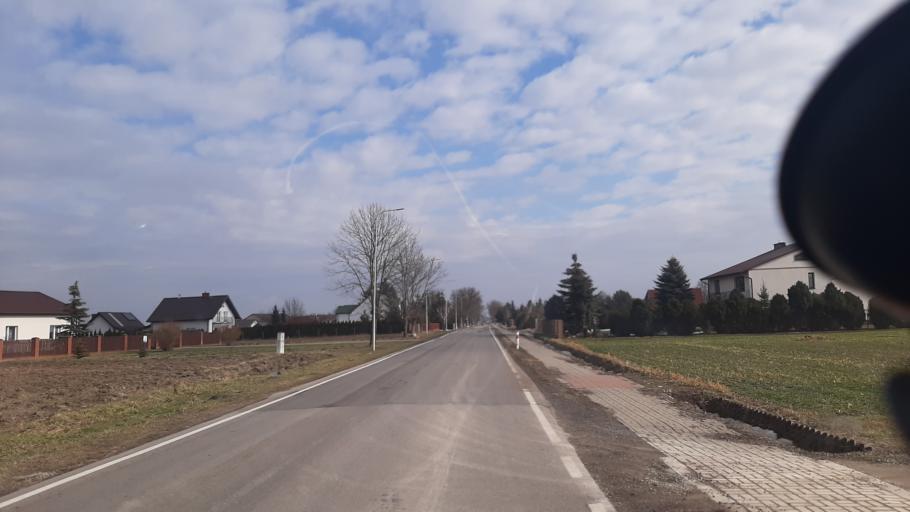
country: PL
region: Lublin Voivodeship
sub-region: Powiat lubelski
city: Niemce
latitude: 51.3614
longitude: 22.5732
